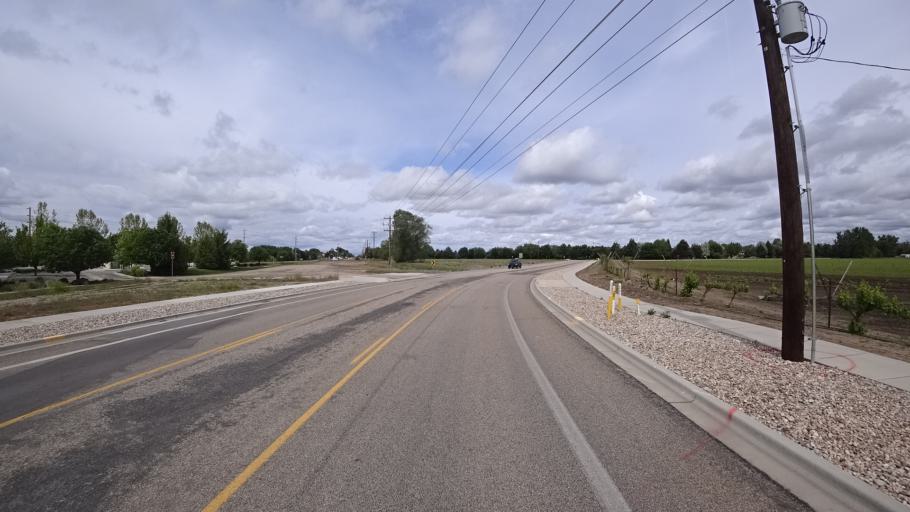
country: US
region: Idaho
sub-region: Ada County
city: Eagle
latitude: 43.6957
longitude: -116.3771
